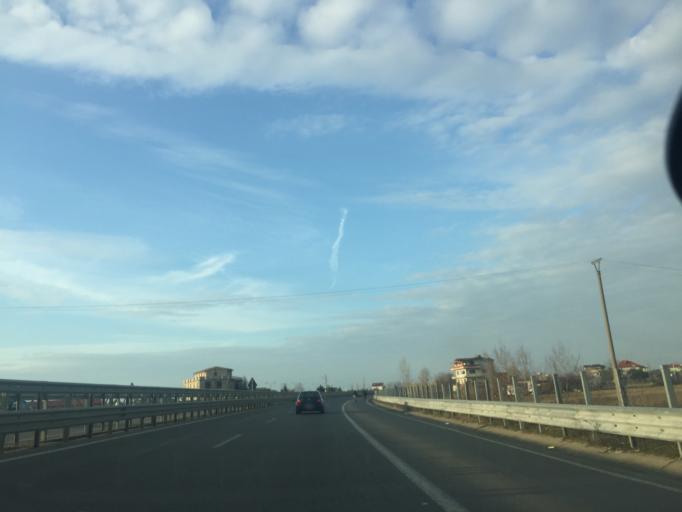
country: AL
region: Durres
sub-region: Rrethi i Krujes
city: Thumane
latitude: 41.5450
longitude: 19.6730
